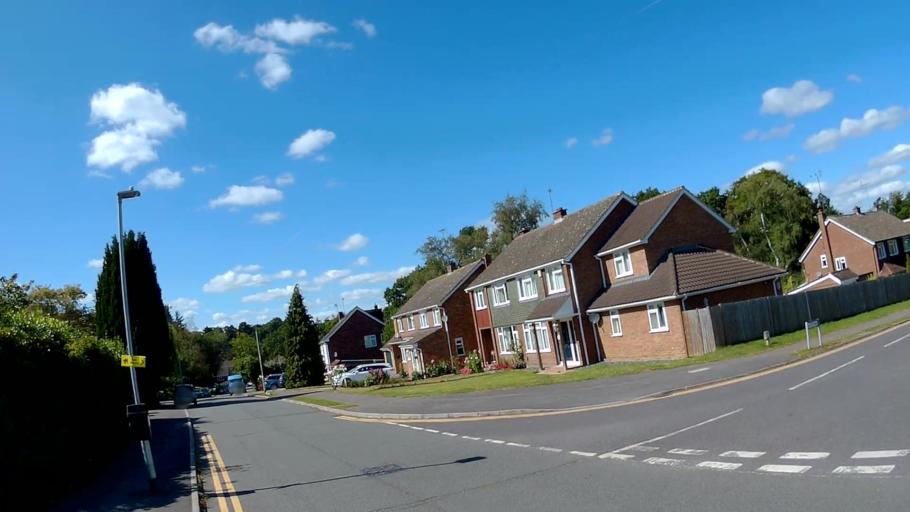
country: GB
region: England
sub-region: Bracknell Forest
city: Crowthorne
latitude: 51.3771
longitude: -0.8007
